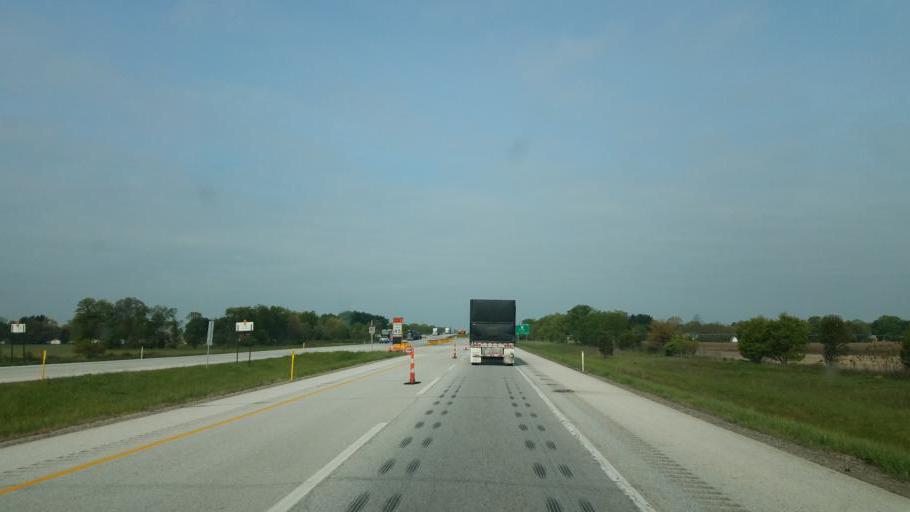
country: US
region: Indiana
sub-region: Elkhart County
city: Simonton Lake
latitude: 41.7304
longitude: -85.9389
